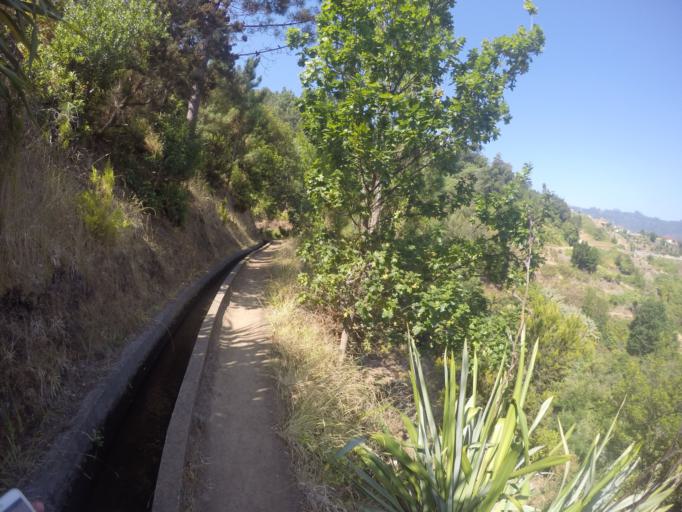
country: PT
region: Madeira
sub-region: Santana
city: Santana
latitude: 32.7557
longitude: -16.8411
